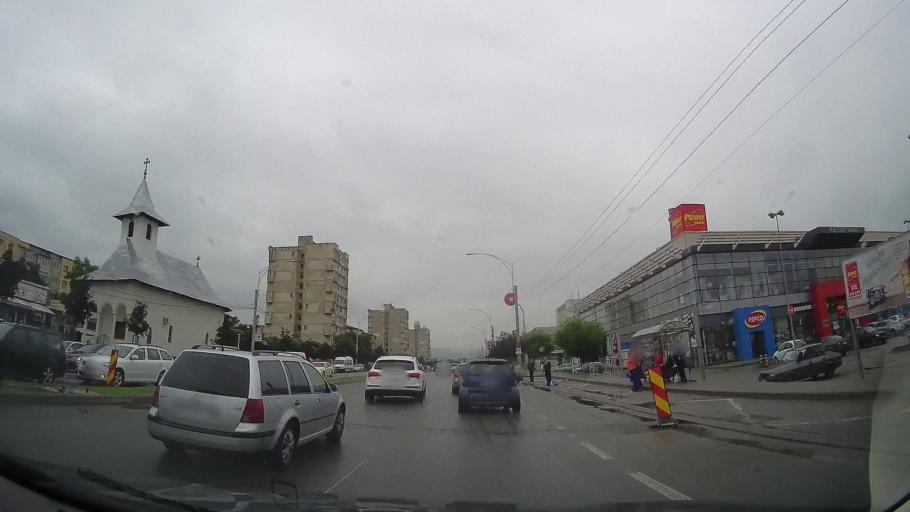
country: RO
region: Mehedinti
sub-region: Municipiul Drobeta-Turnu Severin
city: Drobeta-Turnu Severin
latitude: 44.6325
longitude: 22.6731
